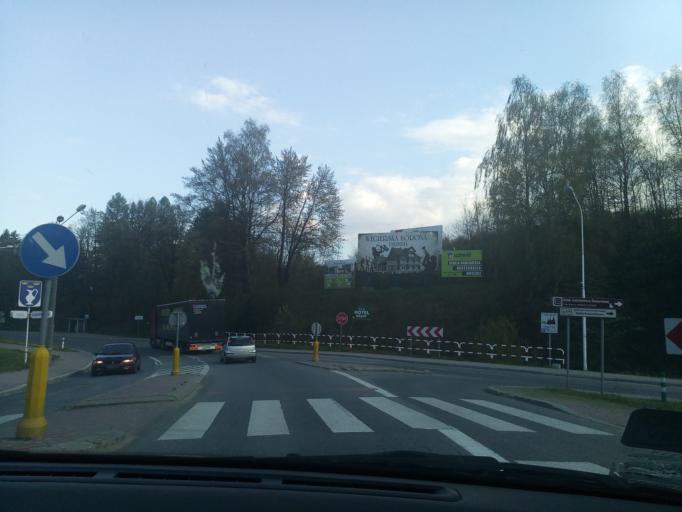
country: PL
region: Lesser Poland Voivodeship
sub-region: Powiat nowosadecki
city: Krynica-Zdroj
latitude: 49.4324
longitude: 20.9500
